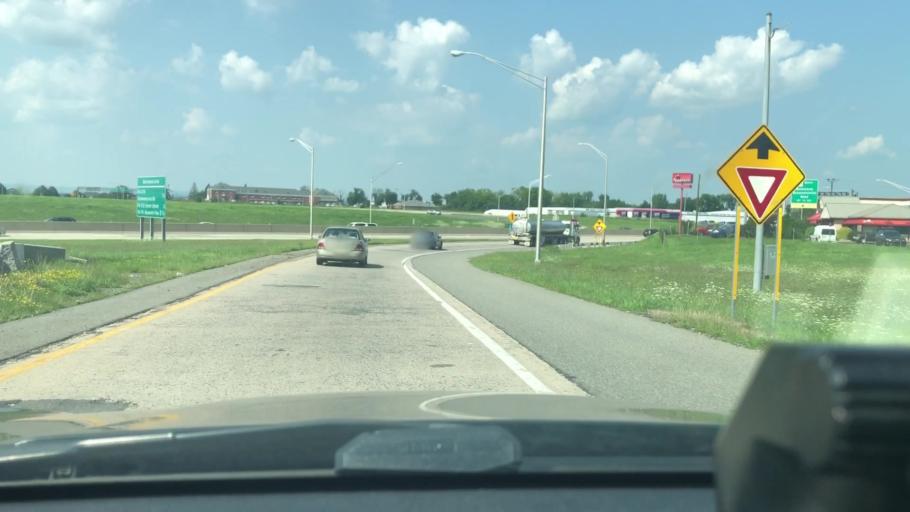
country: US
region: Pennsylvania
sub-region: Lehigh County
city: Fullerton
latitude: 40.6430
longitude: -75.4295
